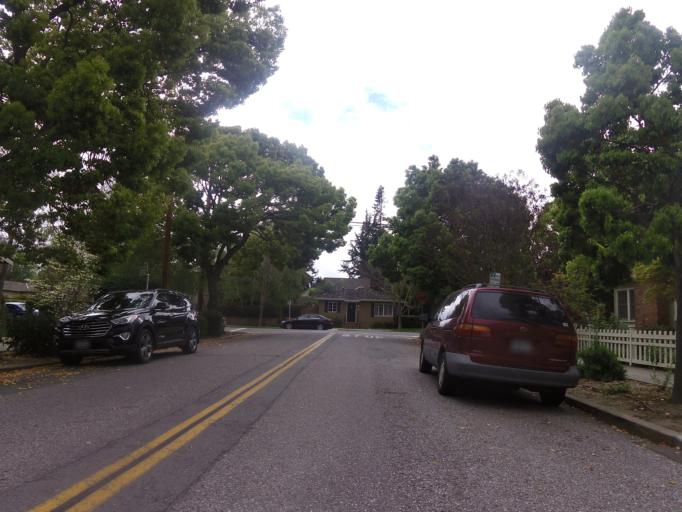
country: US
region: California
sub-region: Santa Clara County
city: Mountain View
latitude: 37.3914
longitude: -122.0768
